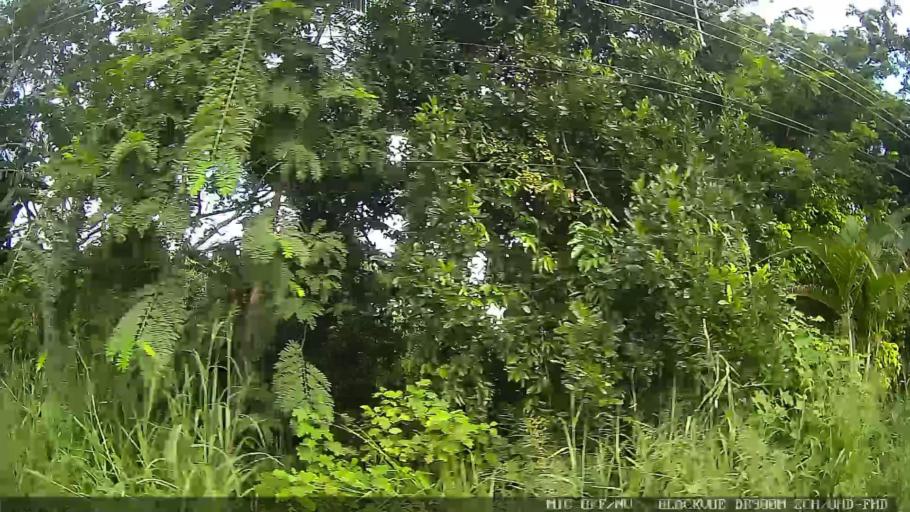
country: BR
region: Sao Paulo
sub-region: Itanhaem
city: Itanhaem
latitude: -24.1948
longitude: -46.8269
